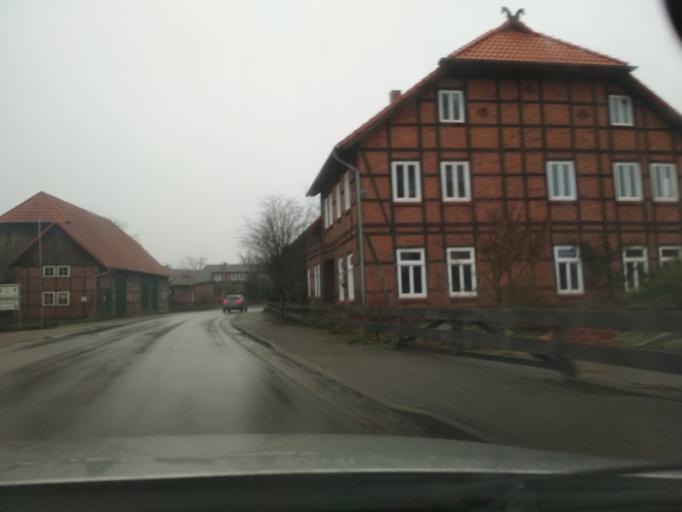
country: DE
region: Lower Saxony
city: Wahrenholz
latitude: 52.6159
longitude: 10.6063
